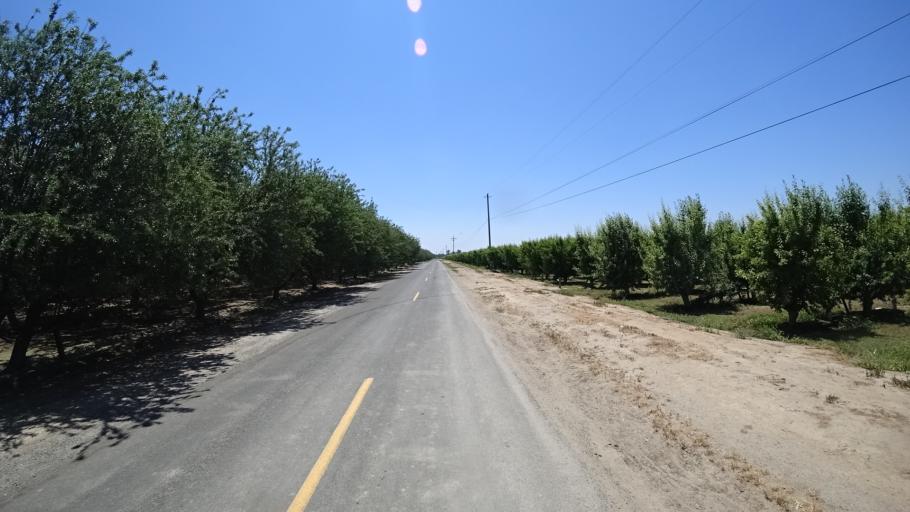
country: US
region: California
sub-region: Fresno County
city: Laton
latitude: 36.4502
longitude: -119.6094
